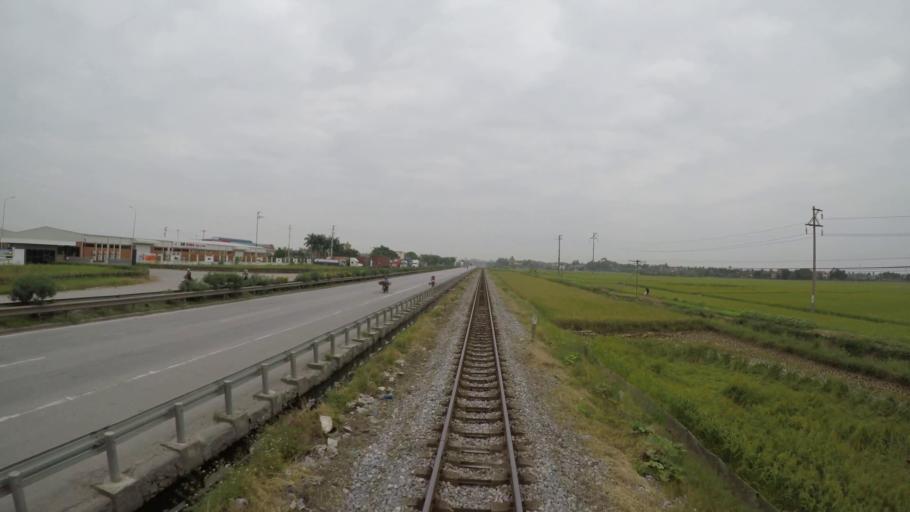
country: VN
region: Hai Duong
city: Phu Thai
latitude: 20.9620
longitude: 106.5192
